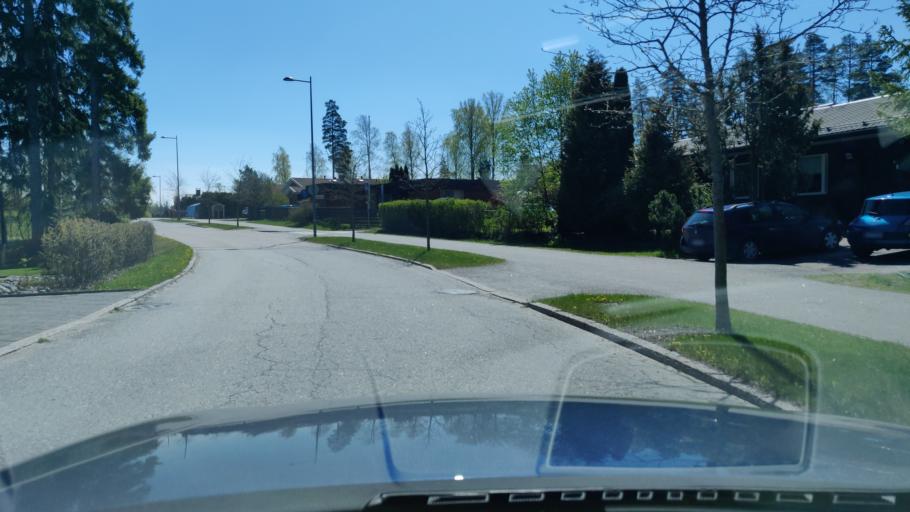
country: FI
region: Uusimaa
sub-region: Helsinki
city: Nurmijaervi
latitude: 60.3634
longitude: 24.7502
